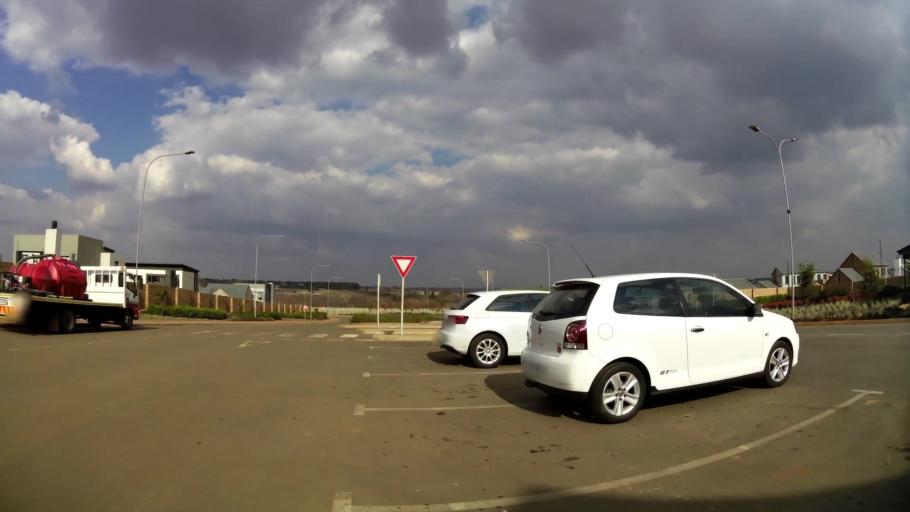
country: ZA
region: Gauteng
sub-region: Ekurhuleni Metropolitan Municipality
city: Tembisa
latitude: -25.9341
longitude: 28.2049
